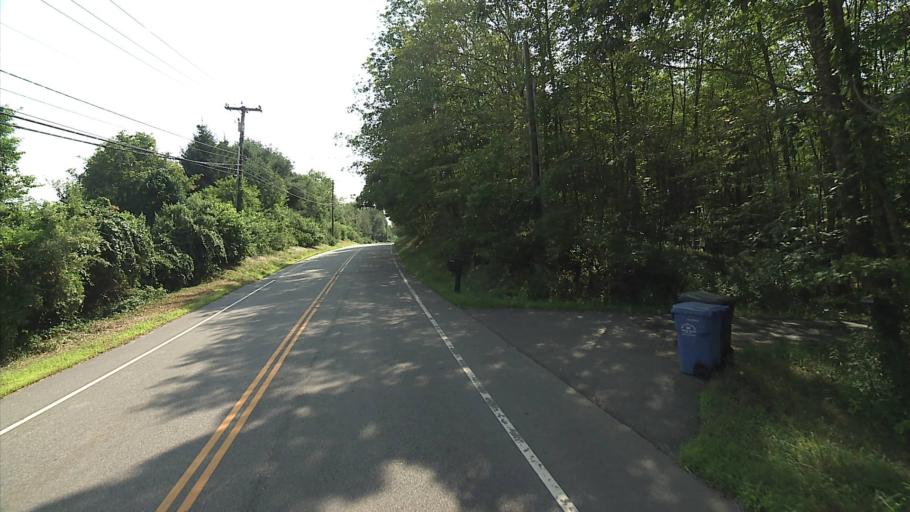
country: US
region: Connecticut
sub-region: New London County
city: Colchester
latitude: 41.5723
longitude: -72.2258
